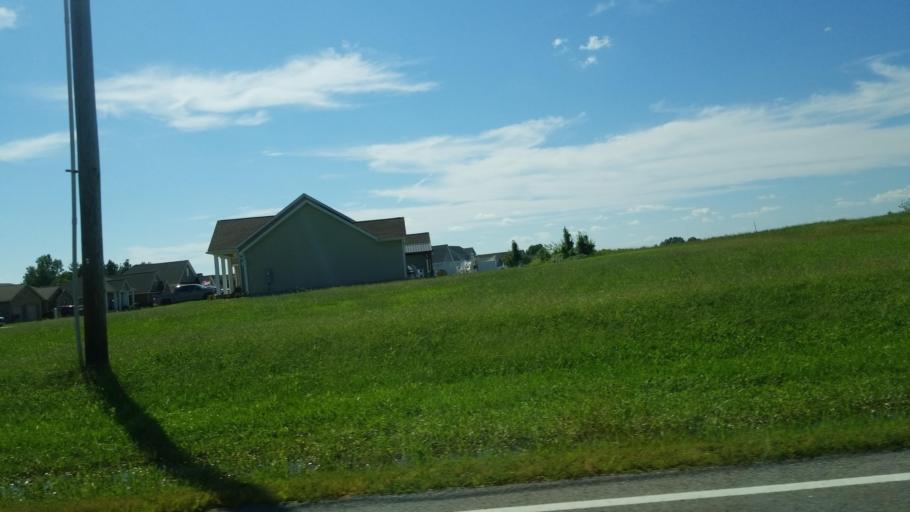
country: US
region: Illinois
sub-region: Williamson County
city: Marion
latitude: 37.7442
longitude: -88.8925
